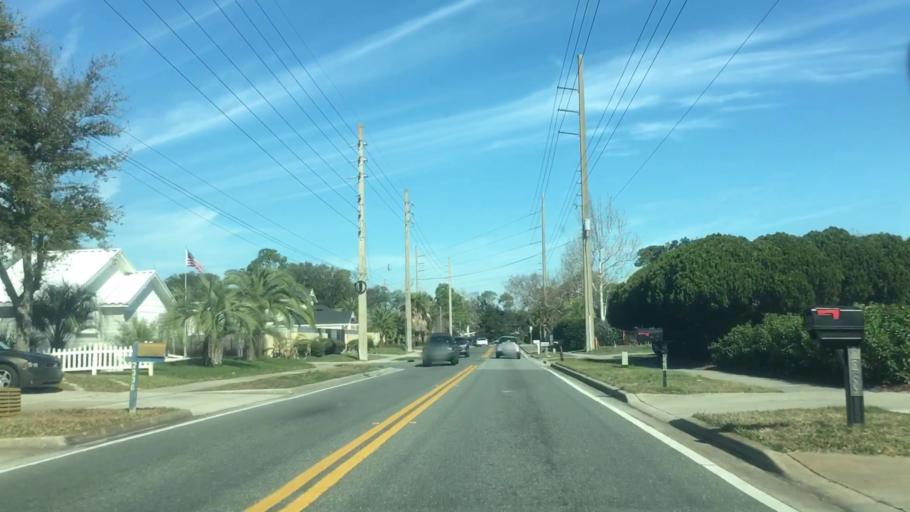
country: US
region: Florida
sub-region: Duval County
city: Jacksonville Beach
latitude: 30.2688
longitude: -81.3948
